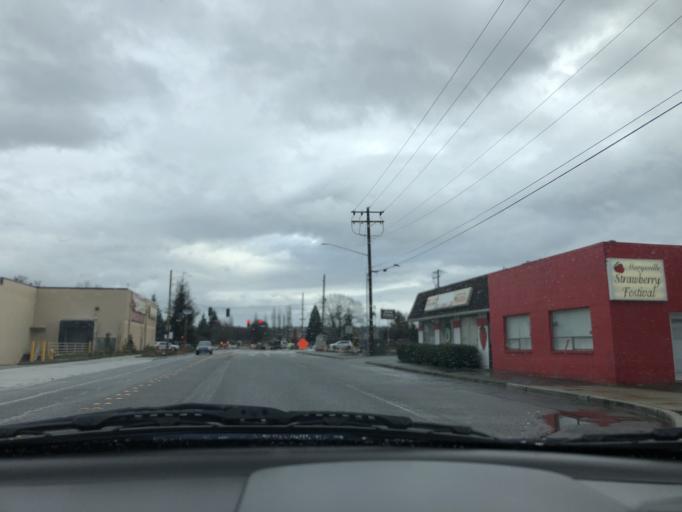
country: US
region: Washington
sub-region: Snohomish County
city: Marysville
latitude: 48.0491
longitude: -122.1785
